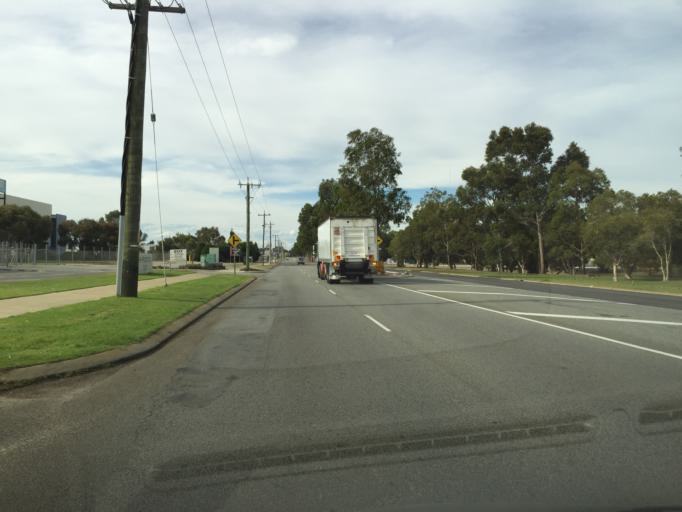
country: AU
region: Western Australia
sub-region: Canning
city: Willetton
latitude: -32.0651
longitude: 115.9011
